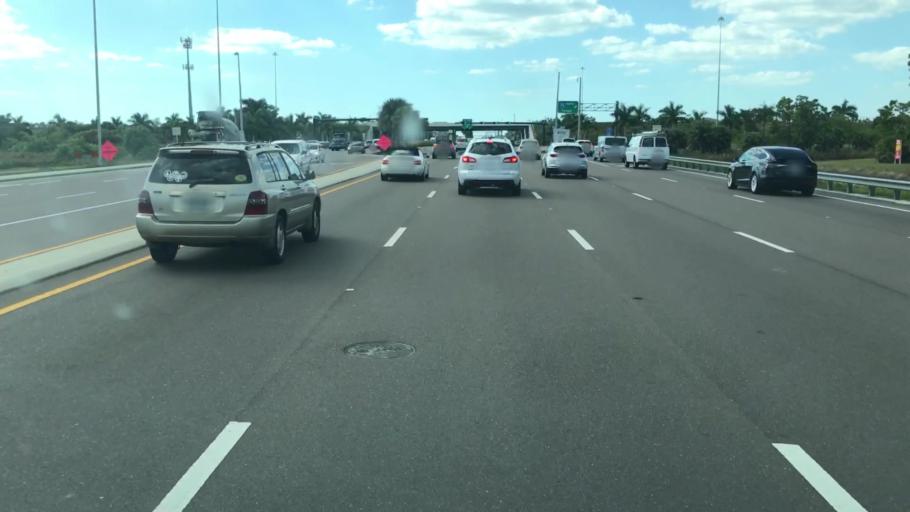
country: US
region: Florida
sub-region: Collier County
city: Vineyards
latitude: 26.2729
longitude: -81.7396
